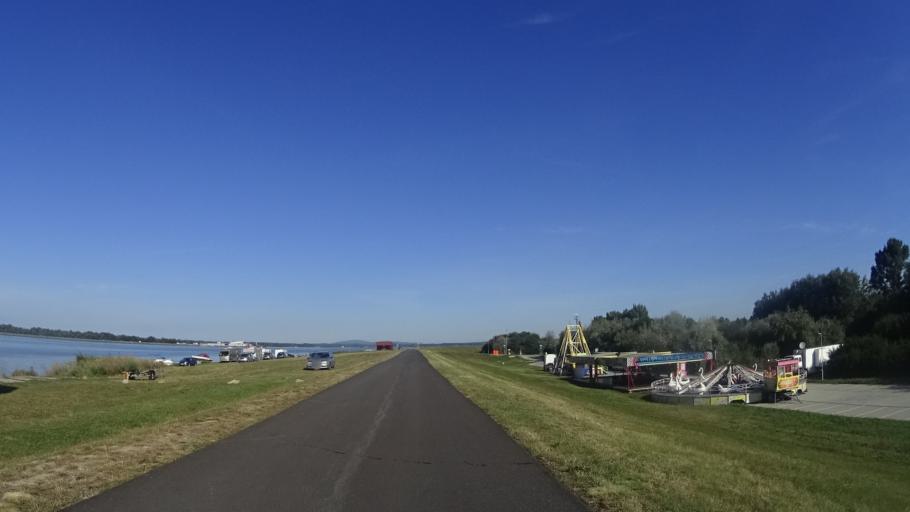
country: SK
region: Bratislavsky
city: Dunajska Luzna
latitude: 48.0322
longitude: 17.2504
